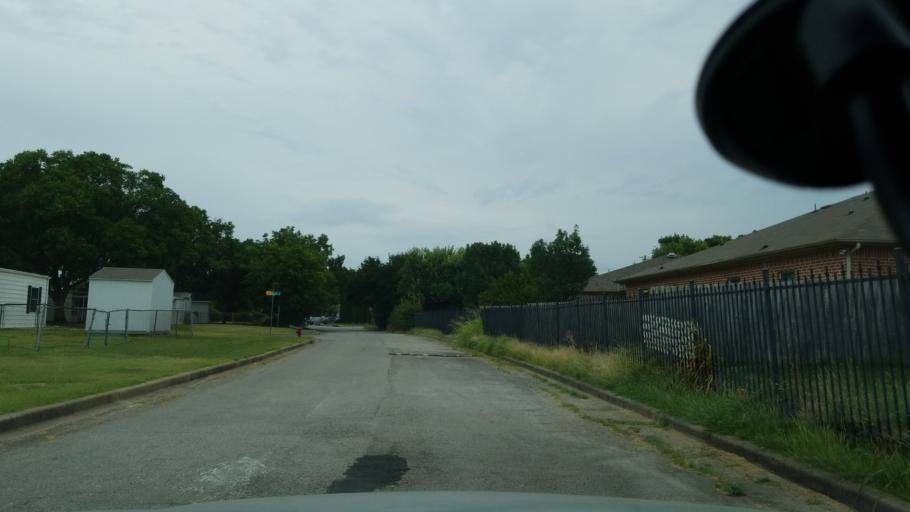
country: US
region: Texas
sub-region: Dallas County
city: Grand Prairie
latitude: 32.7362
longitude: -96.9908
